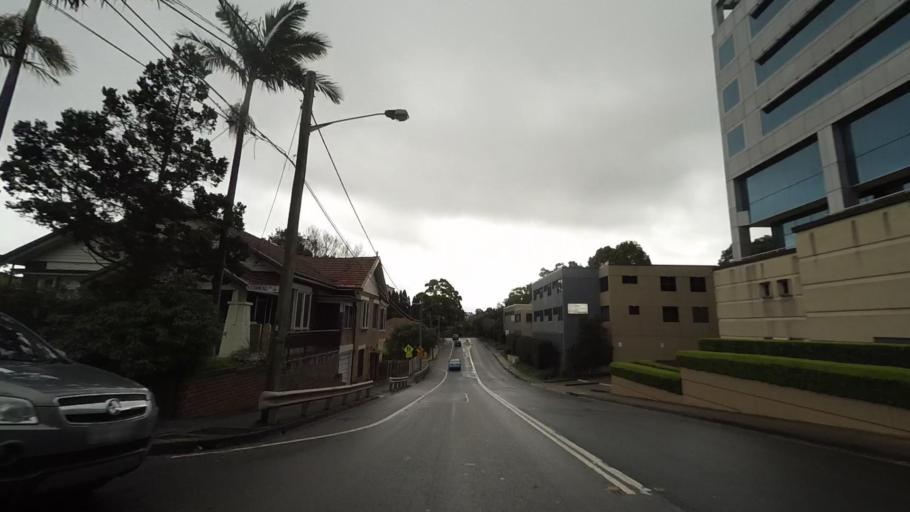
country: AU
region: New South Wales
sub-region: Kogarah
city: Hurstville Grove
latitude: -33.9674
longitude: 151.1007
